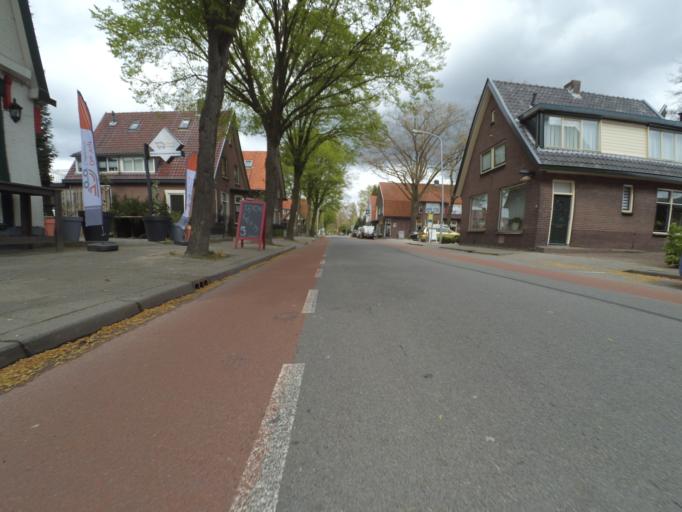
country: NL
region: Gelderland
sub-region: Gemeente Ede
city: Lunteren
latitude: 52.0896
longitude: 5.6186
